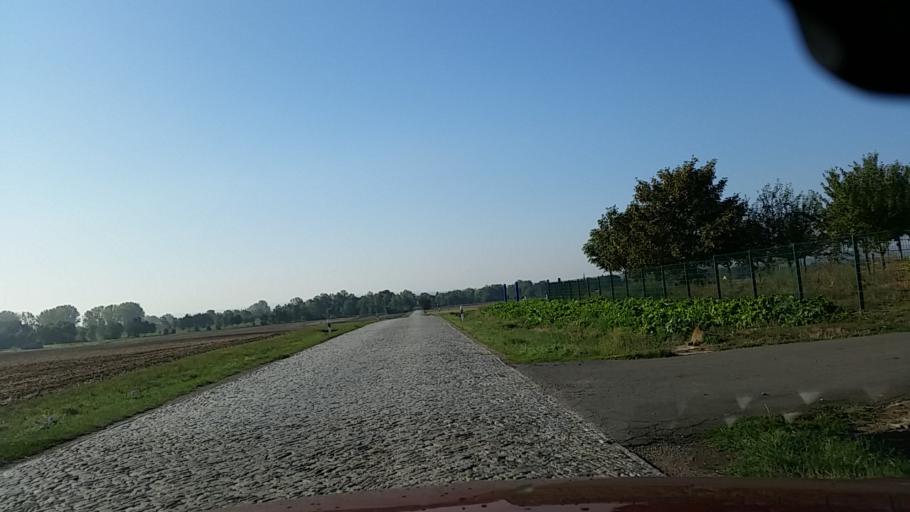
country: DE
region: Thuringia
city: Kolleda
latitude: 51.2013
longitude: 11.2540
